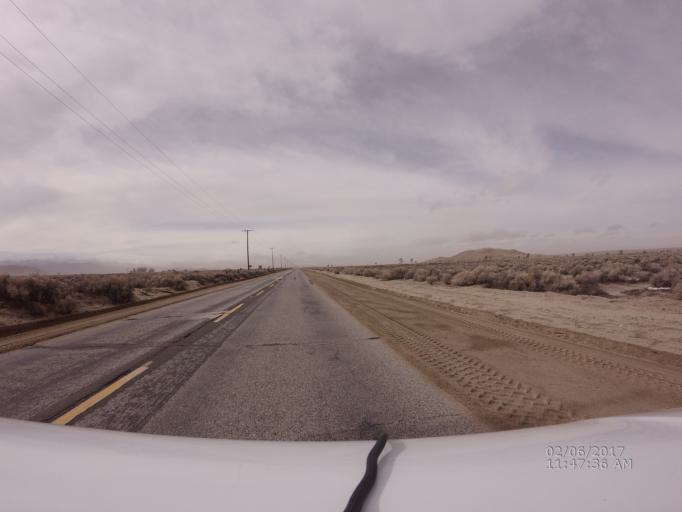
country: US
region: California
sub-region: Los Angeles County
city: Lake Los Angeles
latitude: 34.6020
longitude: -117.6784
